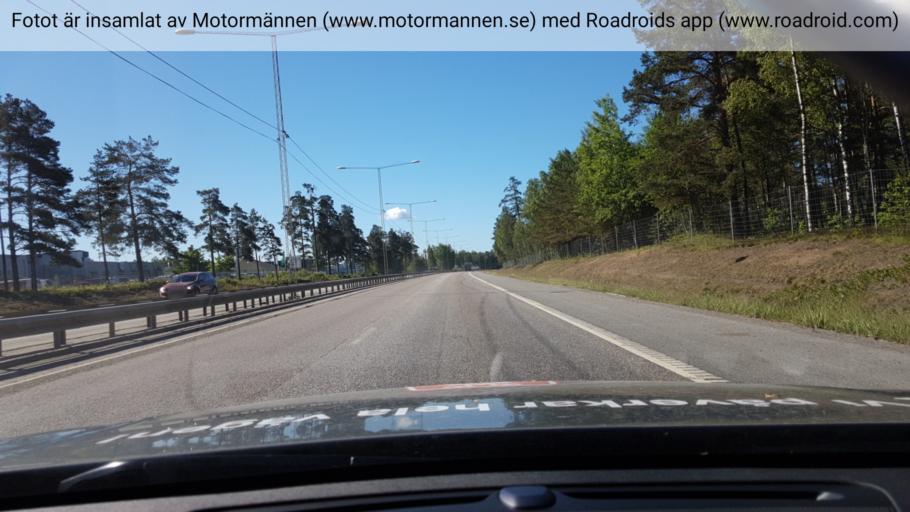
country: SE
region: Stockholm
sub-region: Haninge Kommun
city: Haninge
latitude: 59.1677
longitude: 18.1595
